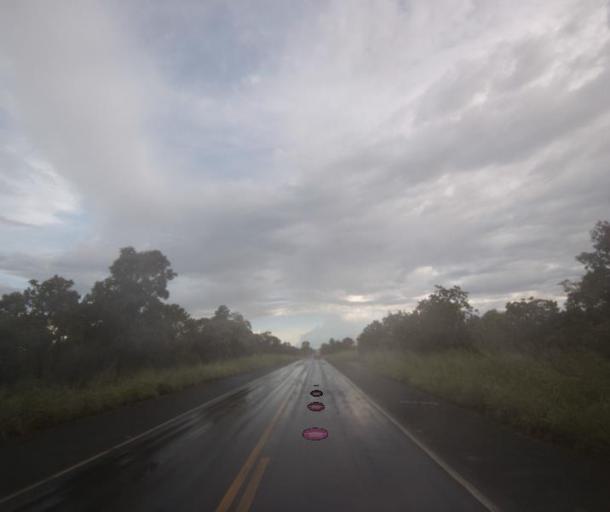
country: BR
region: Goias
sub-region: Porangatu
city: Porangatu
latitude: -13.8330
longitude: -49.0441
